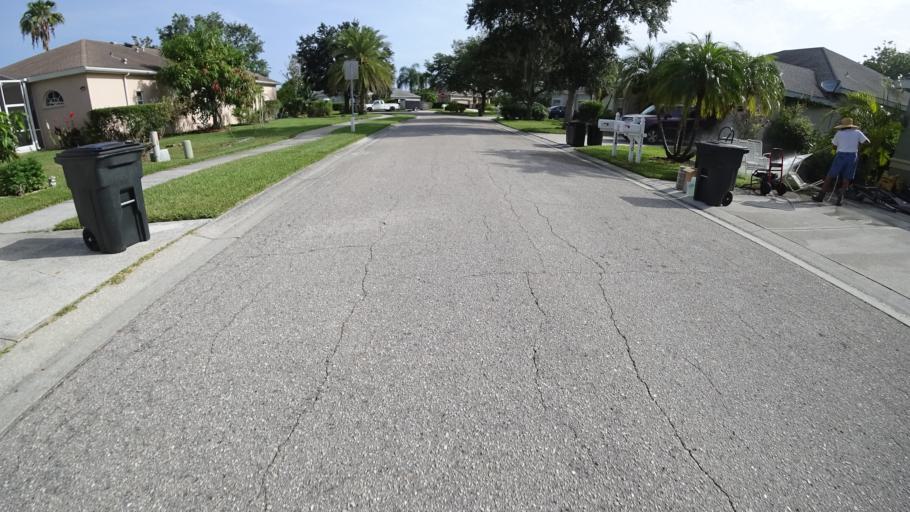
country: US
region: Florida
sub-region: Manatee County
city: Ellenton
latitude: 27.5487
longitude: -82.5004
